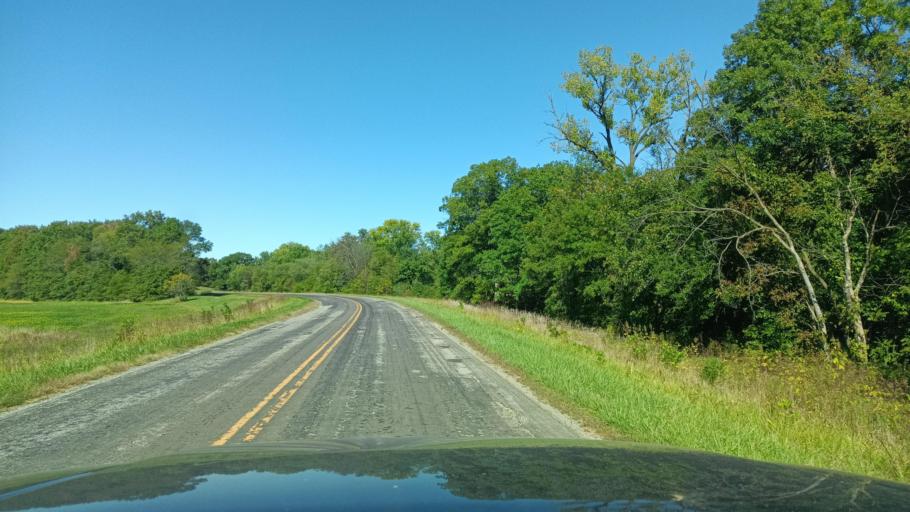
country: US
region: Missouri
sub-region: Scotland County
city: Memphis
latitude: 40.3539
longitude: -92.2468
